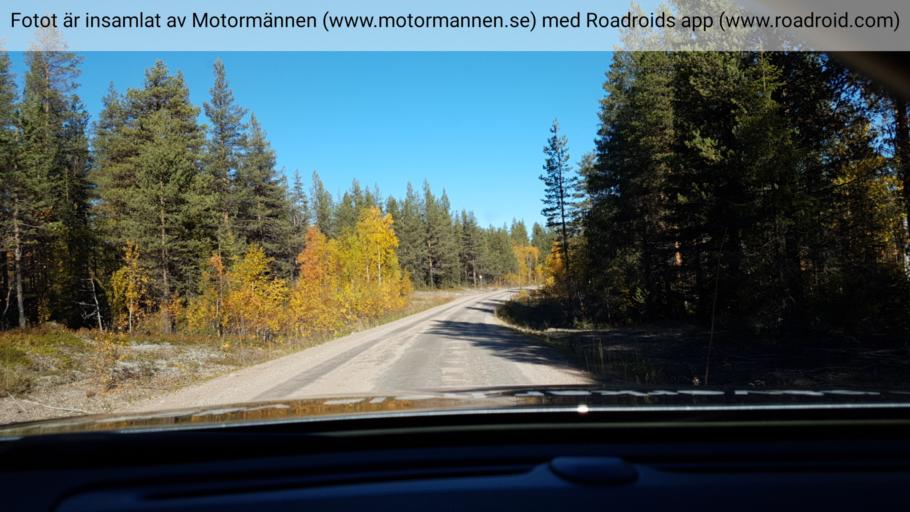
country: SE
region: Norrbotten
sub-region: Gallivare Kommun
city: Gaellivare
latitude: 66.7208
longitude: 20.8958
